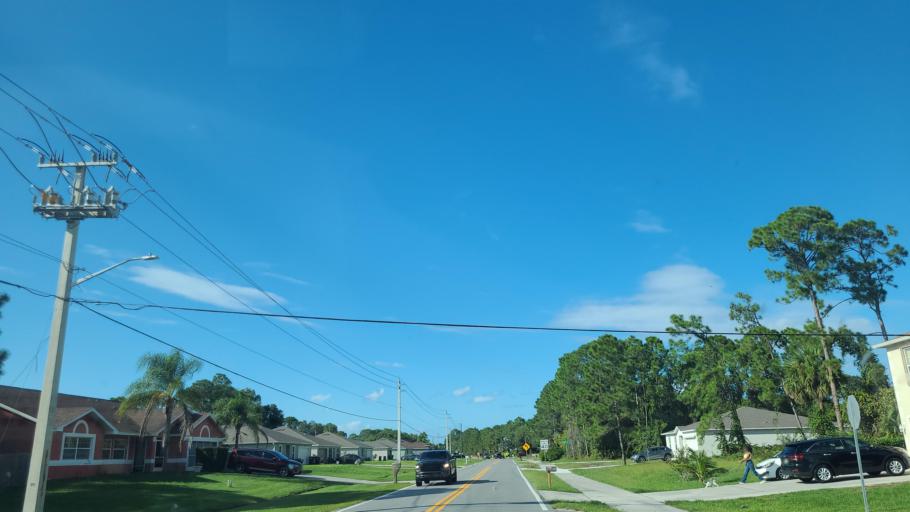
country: US
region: Florida
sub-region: Brevard County
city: Grant-Valkaria
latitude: 27.9702
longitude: -80.6609
